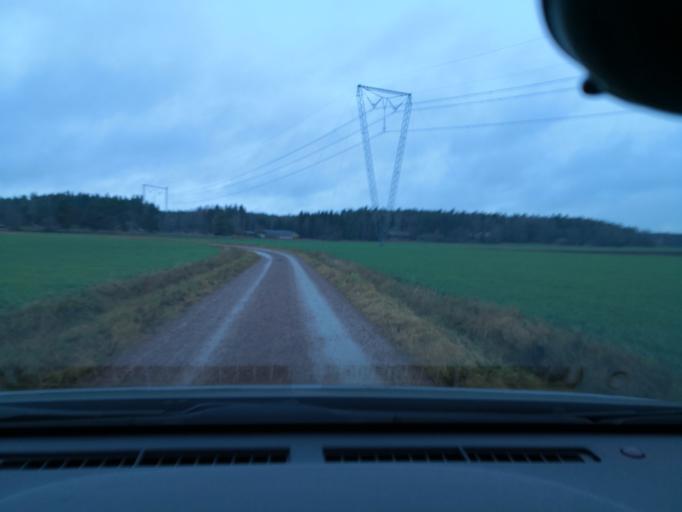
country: SE
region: Vaestmanland
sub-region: Hallstahammars Kommun
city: Hallstahammar
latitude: 59.5637
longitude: 16.1751
